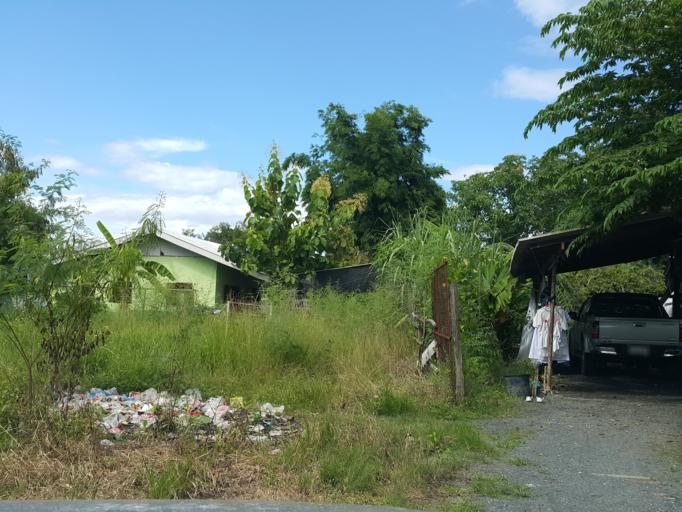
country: TH
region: Chiang Mai
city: San Kamphaeng
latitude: 18.7811
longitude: 99.1289
